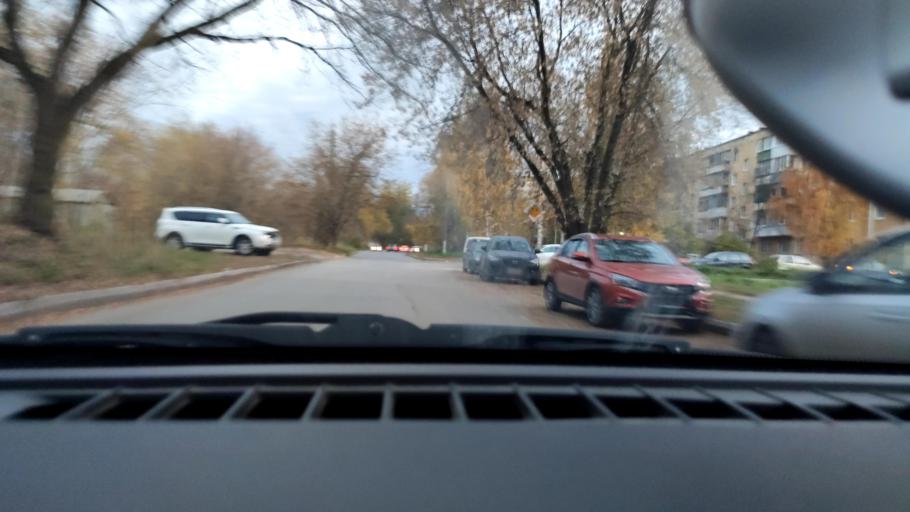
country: RU
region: Perm
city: Perm
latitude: 57.9951
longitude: 56.2004
